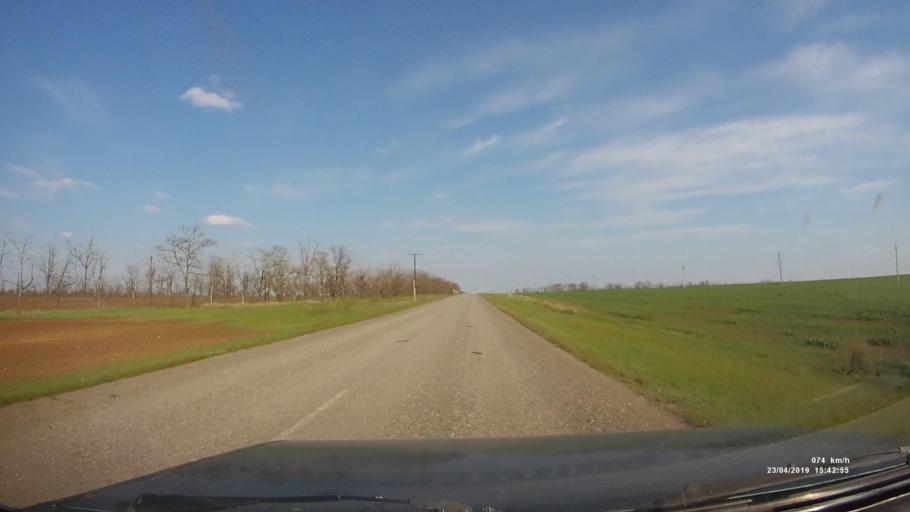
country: RU
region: Rostov
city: Remontnoye
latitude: 46.5465
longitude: 43.0745
